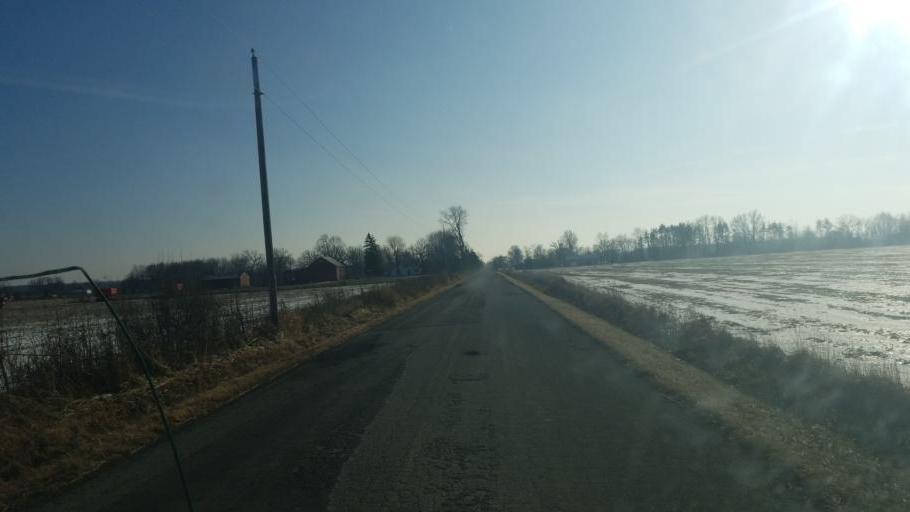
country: US
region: Ohio
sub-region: Morrow County
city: Cardington
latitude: 40.4738
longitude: -82.8698
